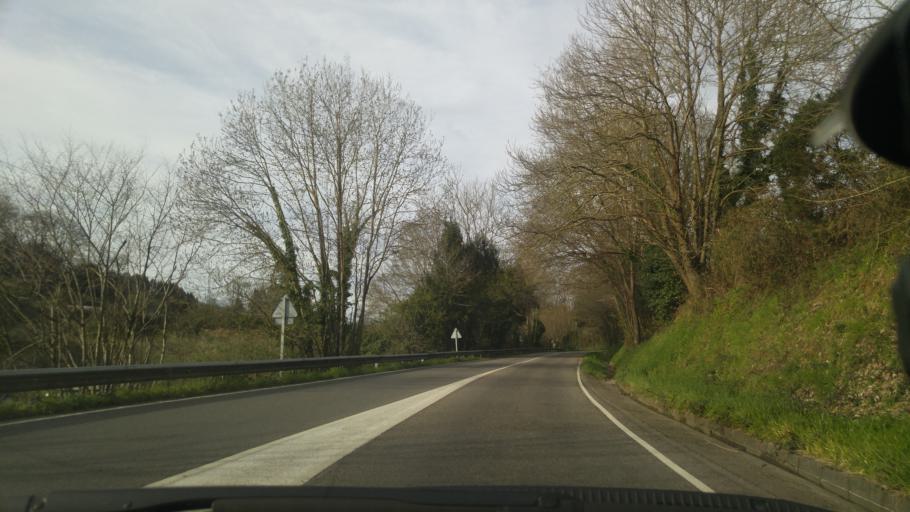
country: ES
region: Asturias
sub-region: Province of Asturias
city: Llanera
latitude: 43.4598
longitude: -5.8514
